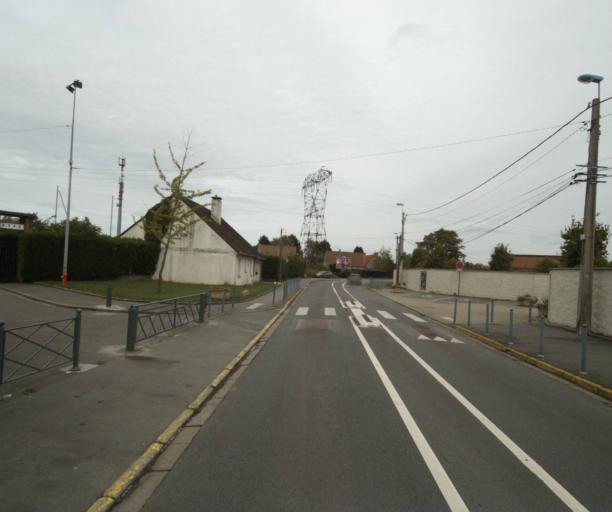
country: FR
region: Nord-Pas-de-Calais
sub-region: Departement du Nord
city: Faches-Thumesnil
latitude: 50.5916
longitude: 3.0759
